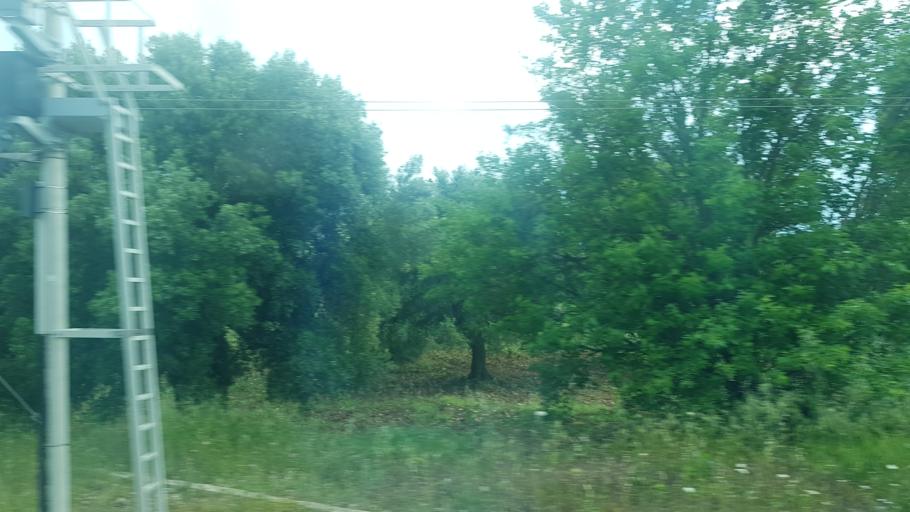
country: IT
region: Apulia
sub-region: Provincia di Brindisi
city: Ostuni
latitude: 40.7538
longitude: 17.5756
